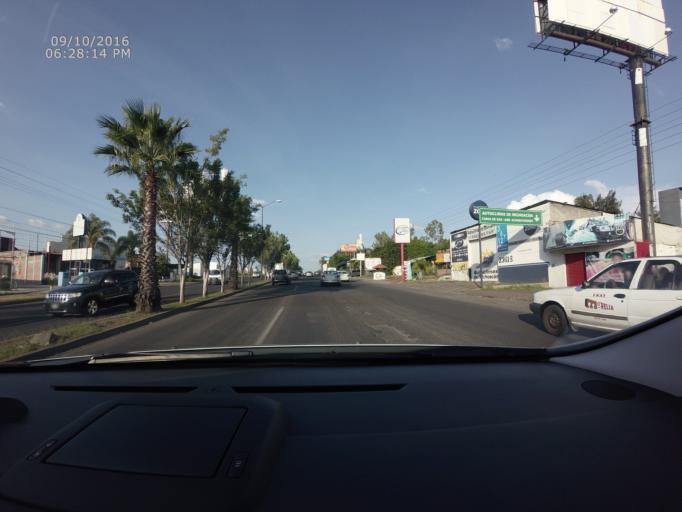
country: MX
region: Michoacan
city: Morelia
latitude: 19.6724
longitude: -101.2080
